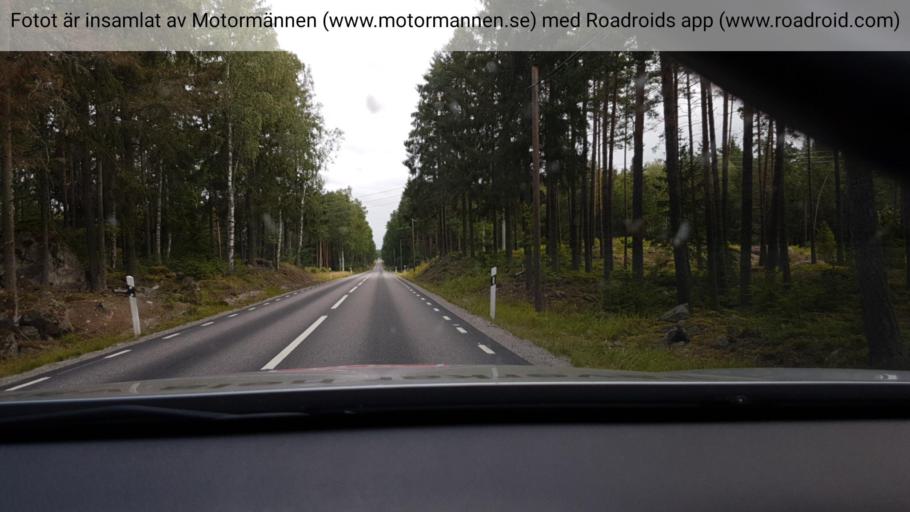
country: SE
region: Stockholm
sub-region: Norrtalje Kommun
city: Rimbo
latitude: 59.7944
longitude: 18.4391
